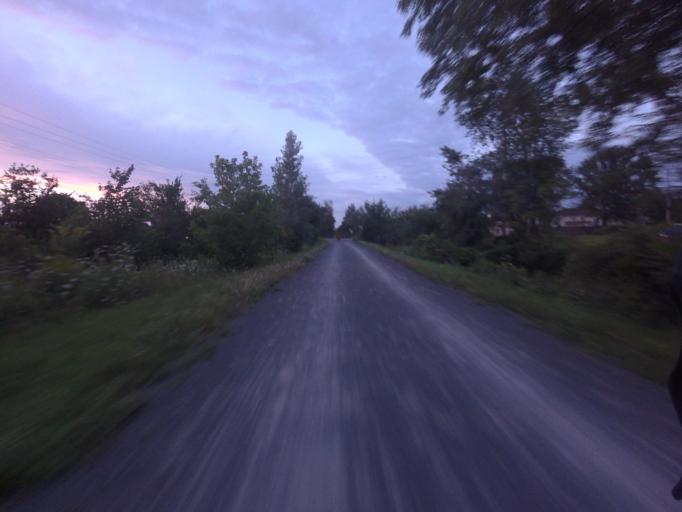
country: CA
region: Ontario
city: Bells Corners
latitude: 45.2914
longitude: -75.8707
